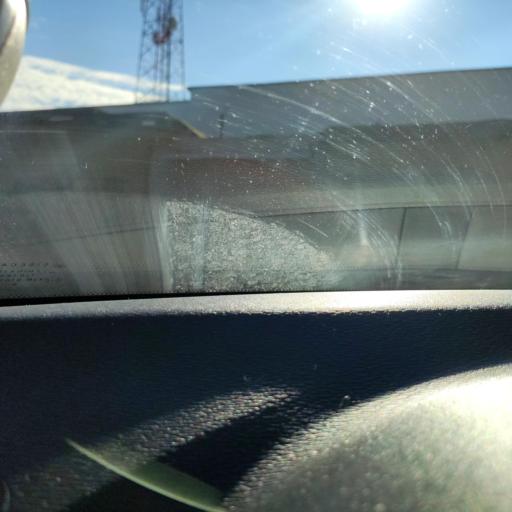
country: RU
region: Samara
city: Petra-Dubrava
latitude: 53.2325
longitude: 50.2974
